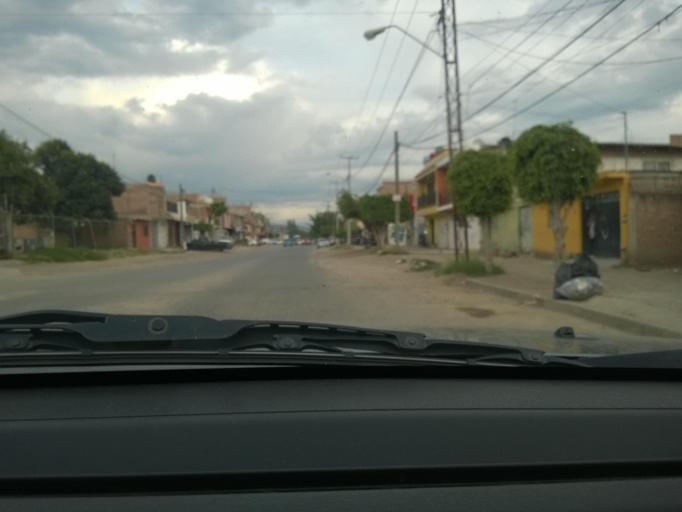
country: MX
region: Guanajuato
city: Leon
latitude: 21.1374
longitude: -101.6473
